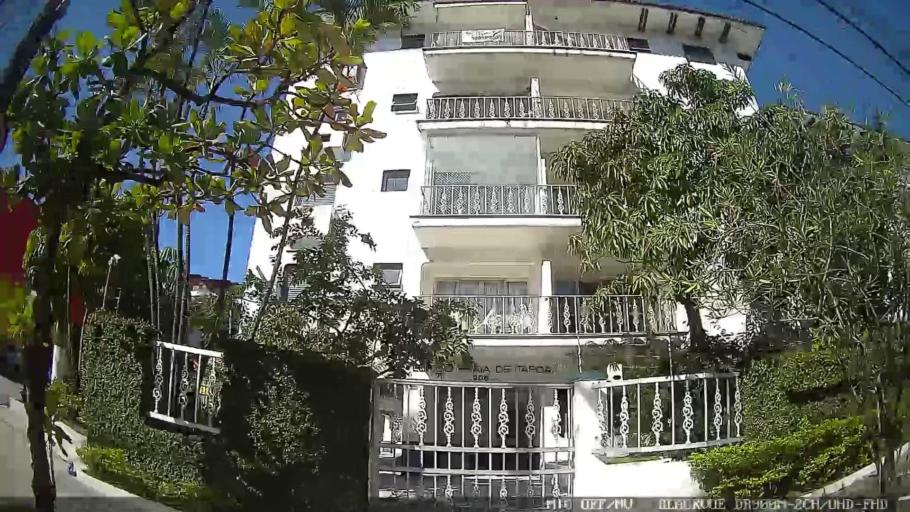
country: BR
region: Sao Paulo
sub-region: Guaruja
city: Guaruja
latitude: -23.9911
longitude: -46.2406
